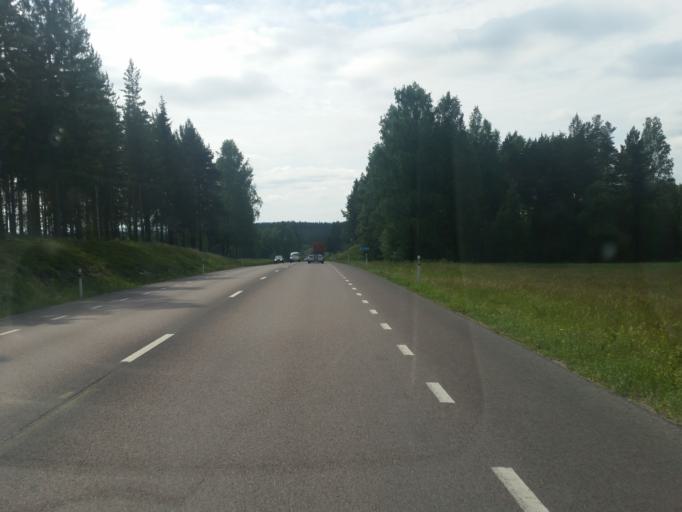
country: SE
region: Dalarna
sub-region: Gagnefs Kommun
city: Gagnef
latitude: 60.6386
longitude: 15.0577
